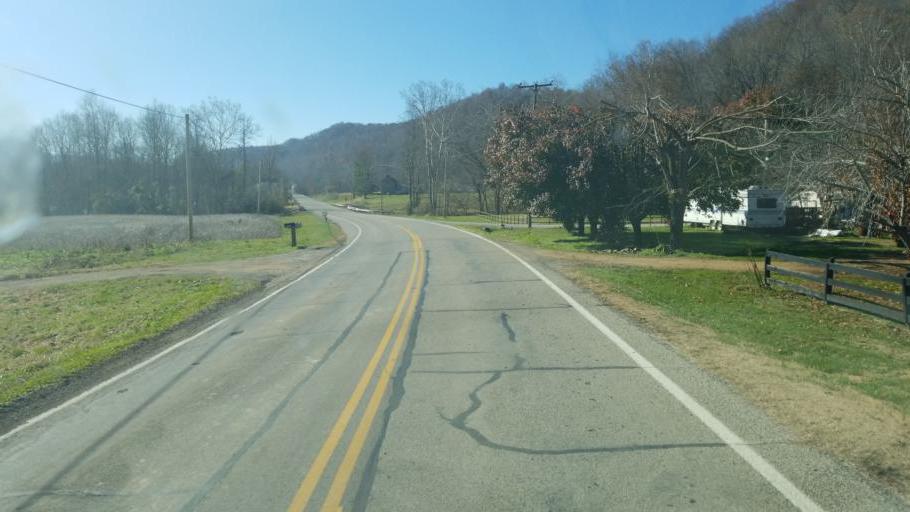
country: US
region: Kentucky
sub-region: Lewis County
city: Vanceburg
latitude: 38.6342
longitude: -83.2498
